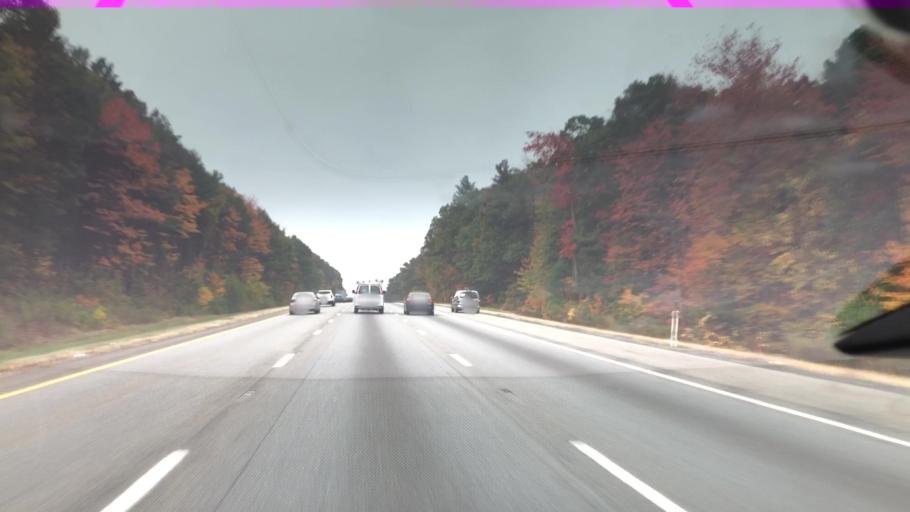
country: US
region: Massachusetts
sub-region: Worcester County
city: Harvard
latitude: 42.5064
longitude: -71.5257
